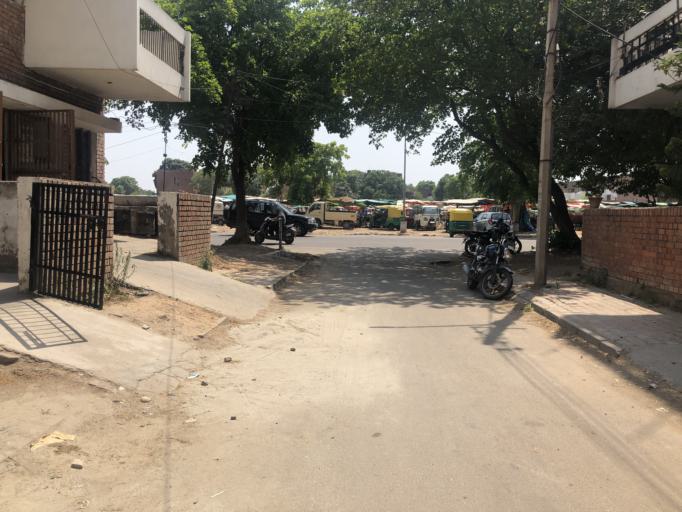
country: IN
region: Chandigarh
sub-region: Chandigarh
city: Chandigarh
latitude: 30.7027
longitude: 76.7647
